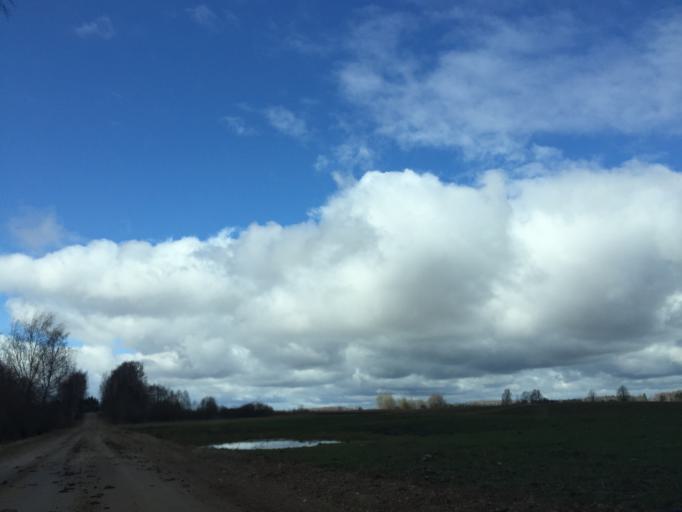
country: LV
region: Akniste
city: Akniste
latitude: 56.0934
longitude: 25.9922
